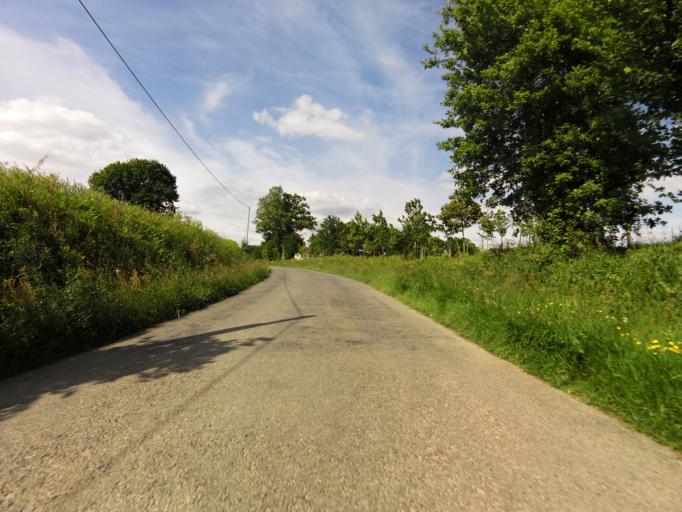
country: FR
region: Brittany
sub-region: Departement du Morbihan
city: Molac
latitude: 47.7281
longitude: -2.4668
